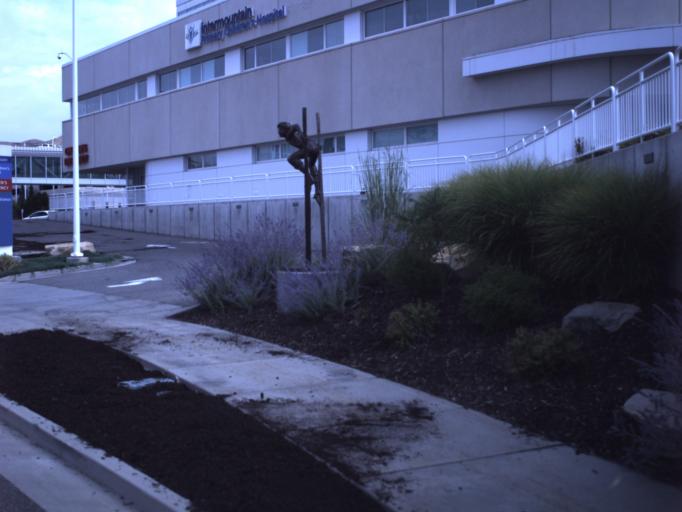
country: US
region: Utah
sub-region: Salt Lake County
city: Salt Lake City
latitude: 40.7707
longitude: -111.8396
